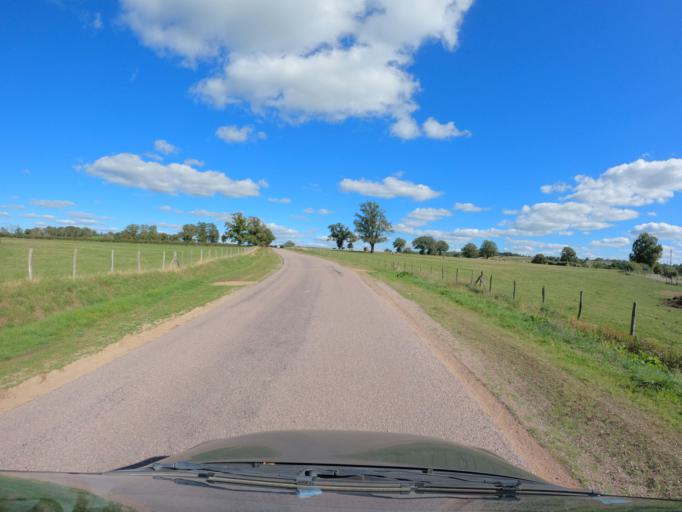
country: FR
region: Auvergne
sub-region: Departement de l'Allier
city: Buxieres-les-Mines
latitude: 46.4027
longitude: 3.0227
